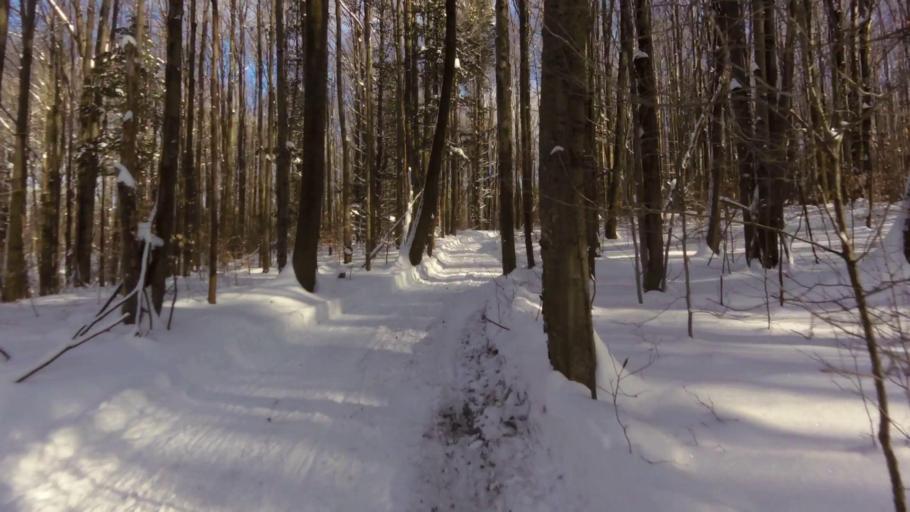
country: US
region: New York
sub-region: Chautauqua County
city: Falconer
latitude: 42.2560
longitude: -79.1434
